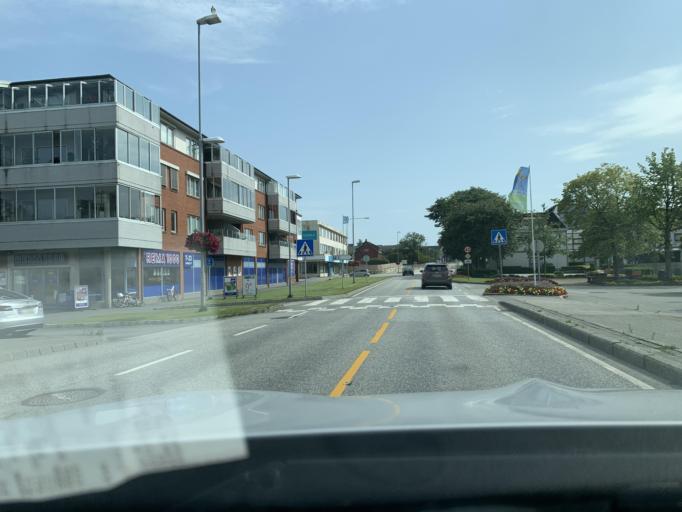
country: NO
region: Rogaland
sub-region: Klepp
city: Kleppe
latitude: 58.7738
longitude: 5.6293
